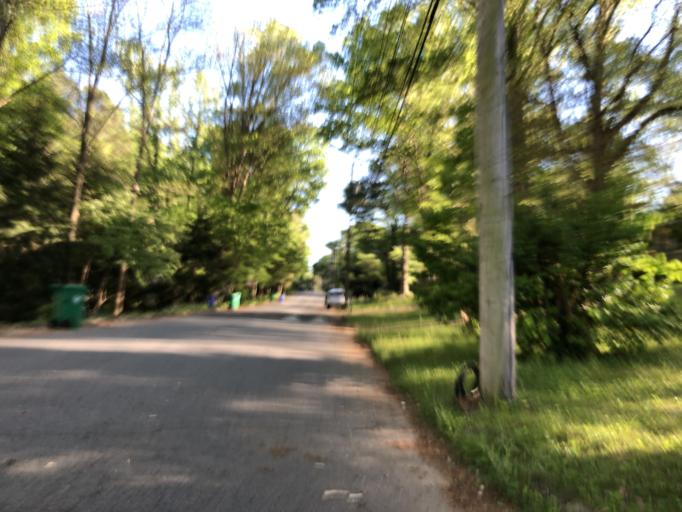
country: US
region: Georgia
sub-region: DeKalb County
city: North Decatur
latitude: 33.8039
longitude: -84.2990
